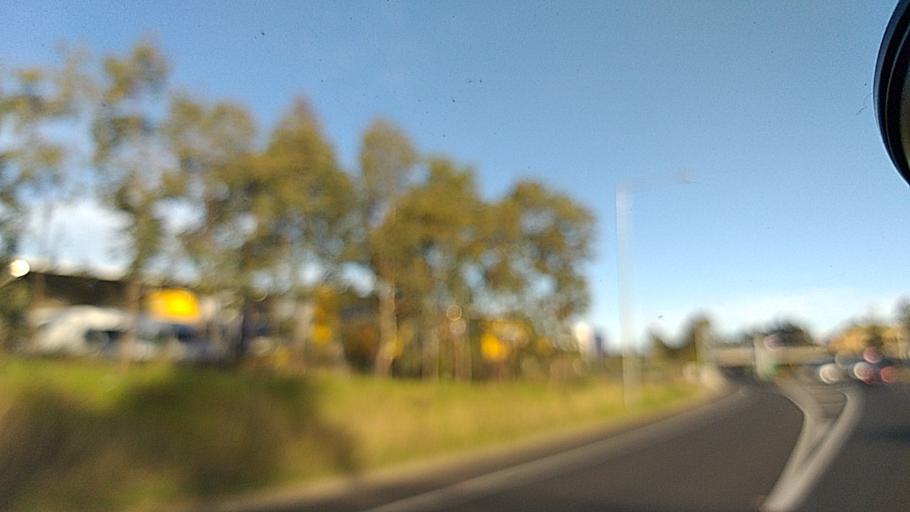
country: AU
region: New South Wales
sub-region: Blacktown
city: Glendenning
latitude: -33.7489
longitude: 150.8460
